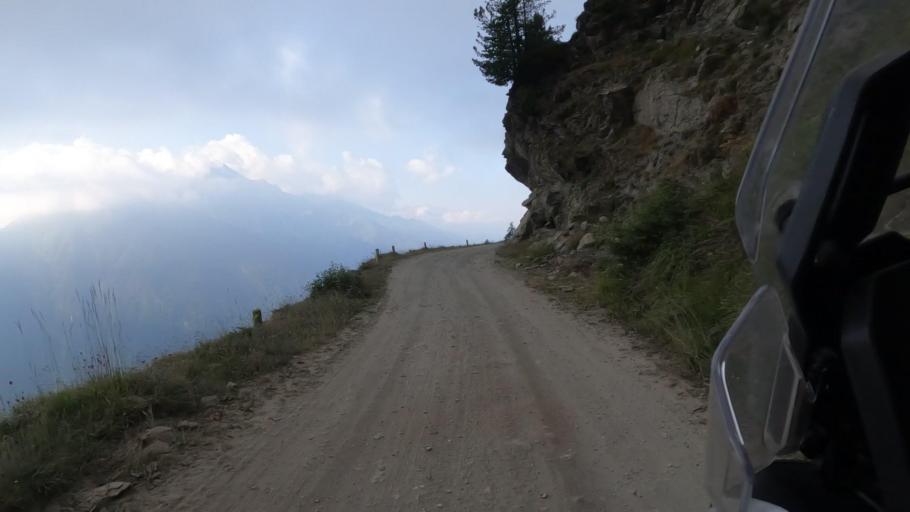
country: IT
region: Piedmont
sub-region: Provincia di Torino
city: Usseaux
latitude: 45.0616
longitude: 6.9950
